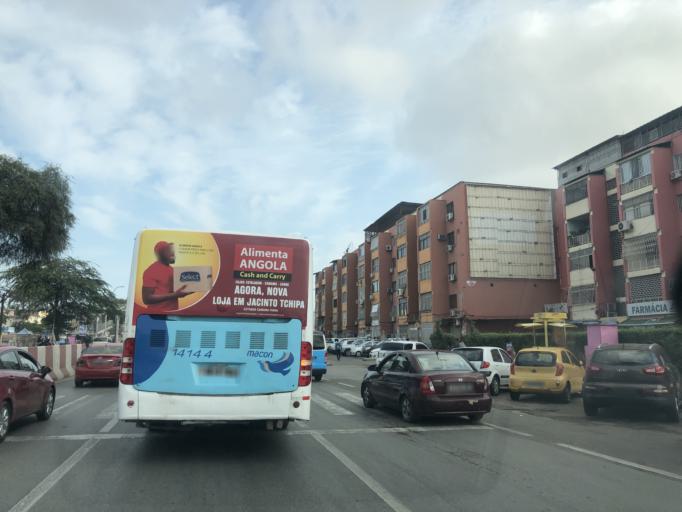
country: AO
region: Luanda
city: Luanda
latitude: -8.8444
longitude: 13.2335
